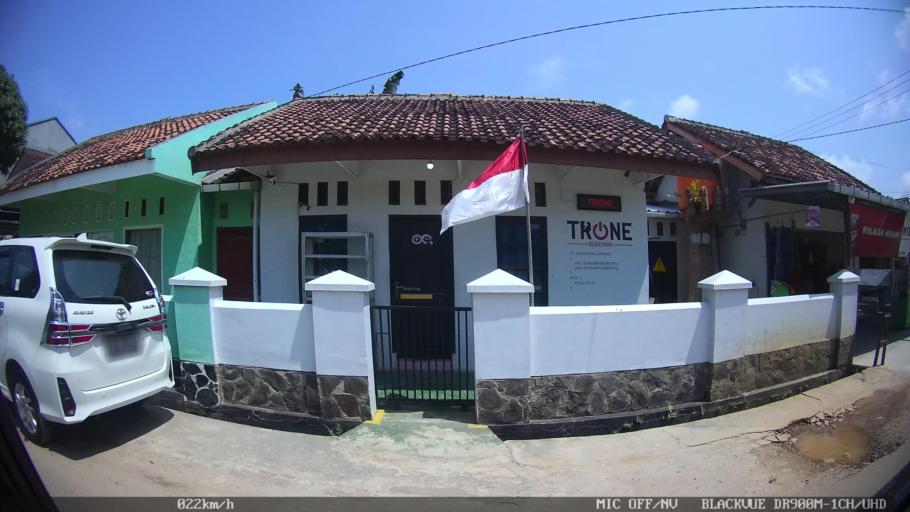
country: ID
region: Lampung
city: Kedaton
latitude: -5.3581
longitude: 105.2766
